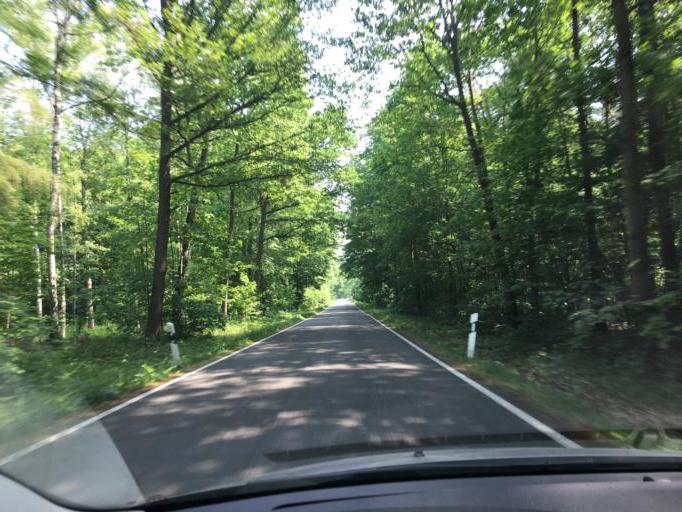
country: DE
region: Saxony
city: Naunhof
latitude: 51.2776
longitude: 12.6147
